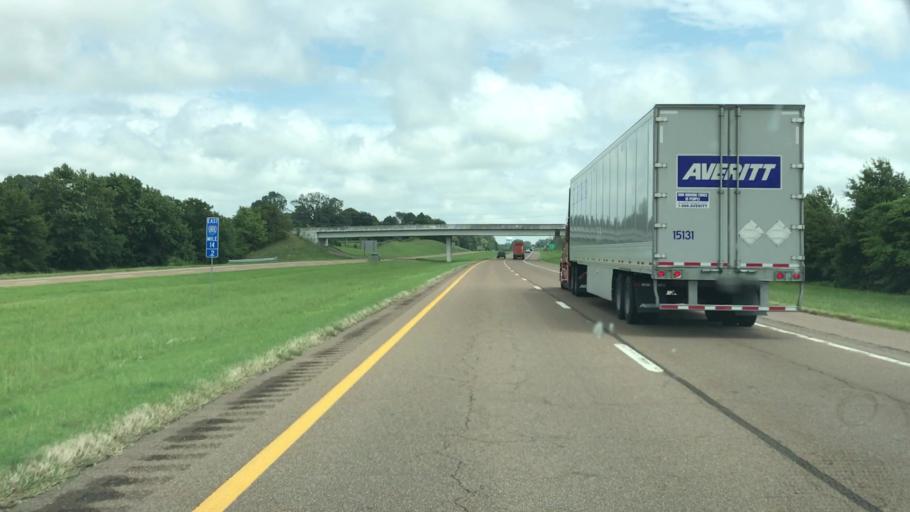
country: US
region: Tennessee
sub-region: Dyer County
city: Dyersburg
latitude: 36.0682
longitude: -89.3744
